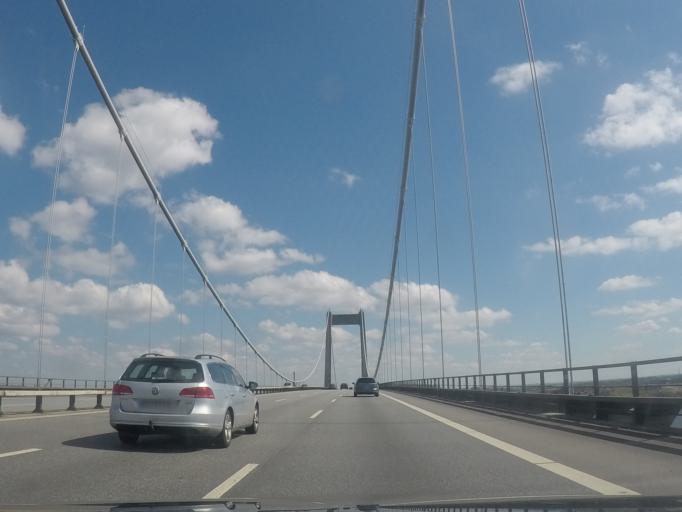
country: DK
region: South Denmark
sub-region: Assens Kommune
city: Vissenbjerg
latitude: 55.3747
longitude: 10.0970
